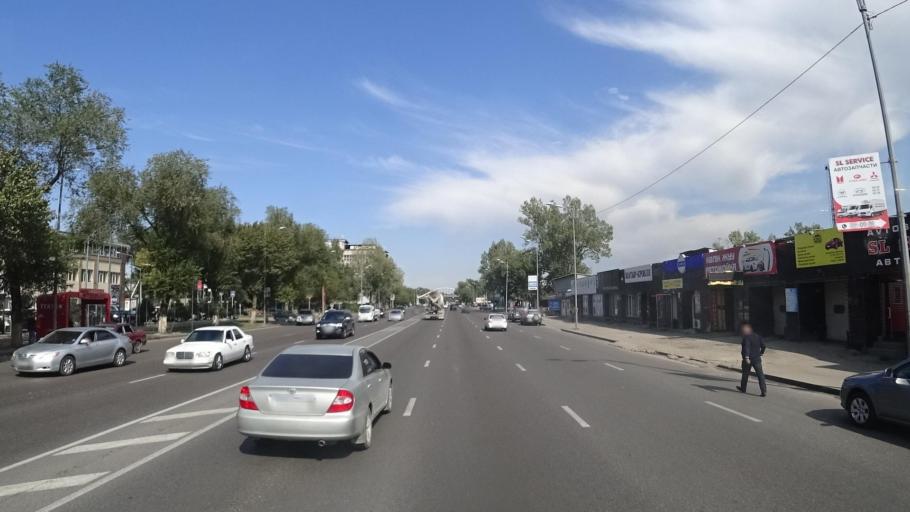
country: KZ
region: Almaty Qalasy
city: Almaty
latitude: 43.2744
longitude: 76.8916
